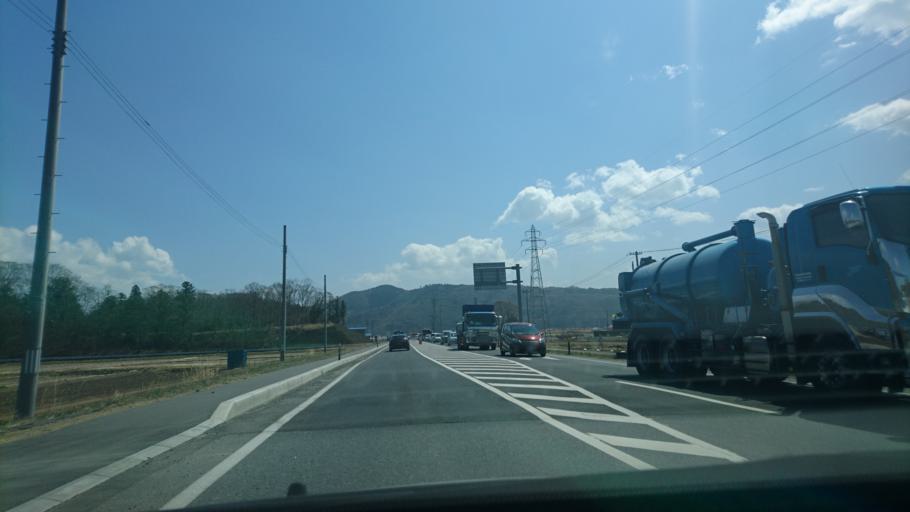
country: JP
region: Miyagi
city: Ishinomaki
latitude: 38.4524
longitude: 141.3132
